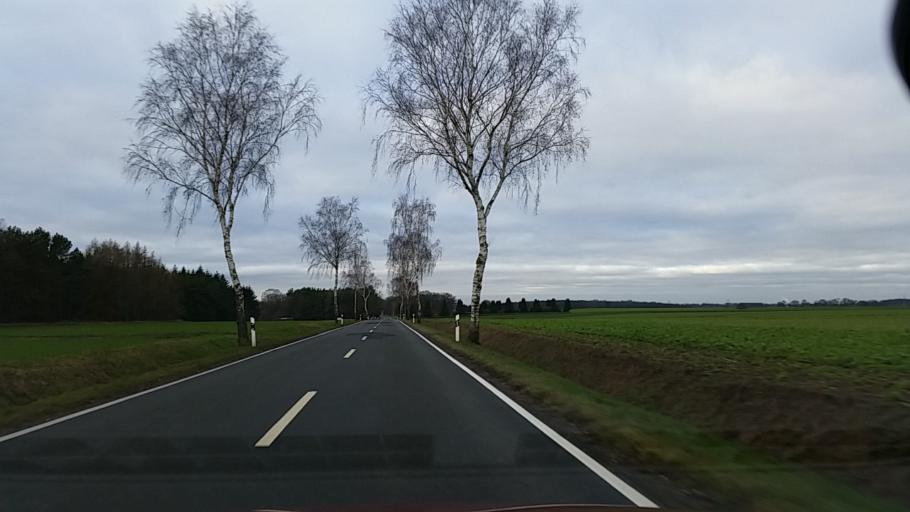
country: DE
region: Lower Saxony
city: Wittingen
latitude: 52.6844
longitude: 10.7751
